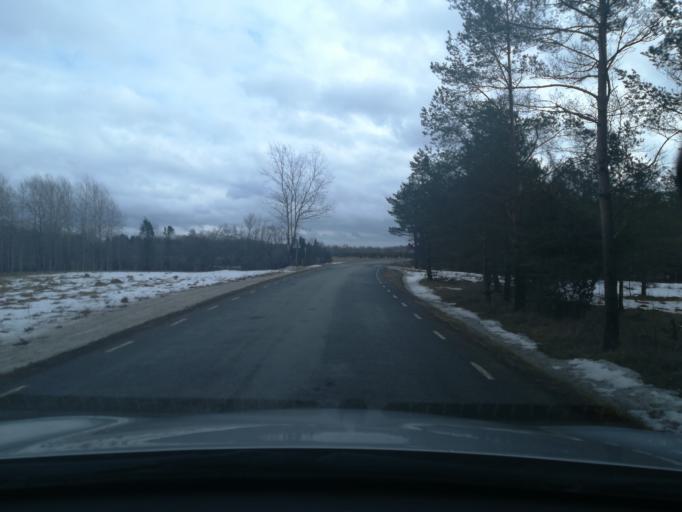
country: EE
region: Harju
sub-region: Saue linn
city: Saue
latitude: 59.3622
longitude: 24.5196
